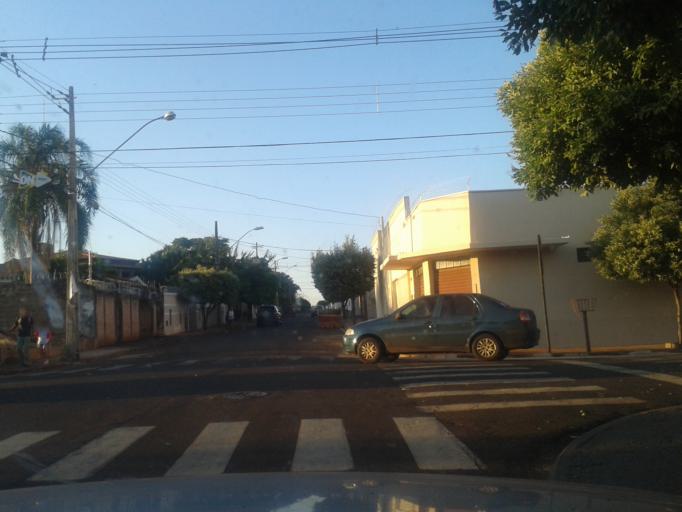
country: BR
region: Minas Gerais
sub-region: Ituiutaba
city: Ituiutaba
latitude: -18.9822
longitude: -49.4645
